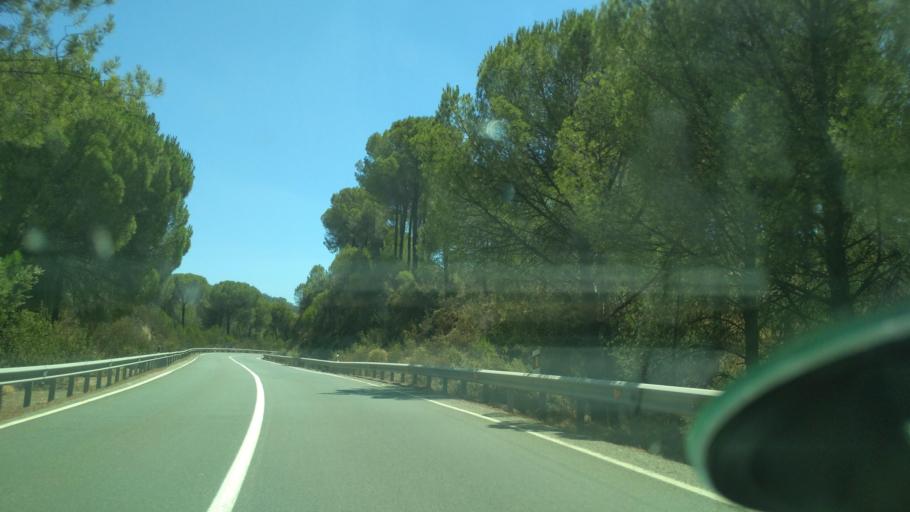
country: ES
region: Andalusia
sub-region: Provincia de Huelva
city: Campofrio
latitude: 37.7507
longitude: -6.5871
